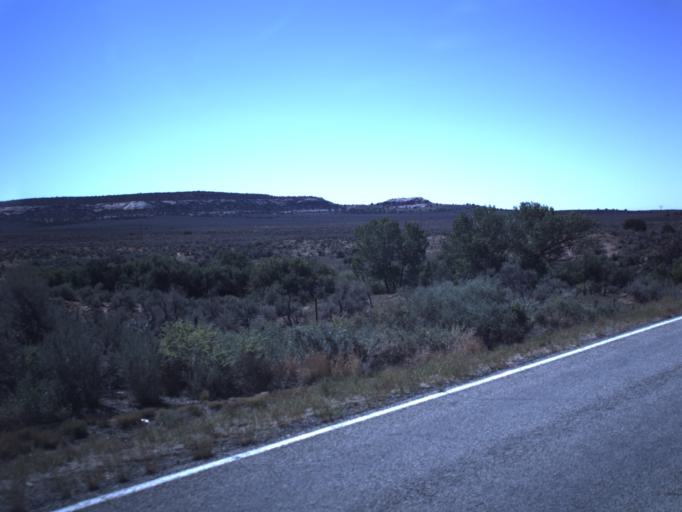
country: US
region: Utah
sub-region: Grand County
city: Moab
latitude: 38.3047
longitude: -109.3696
